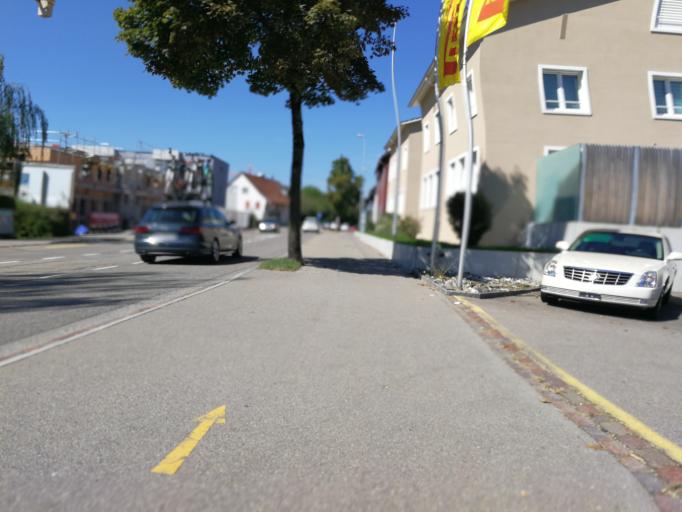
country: CH
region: Zurich
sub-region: Bezirk Pfaeffikon
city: Pfaeffikon / Irgenhausen
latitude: 47.3604
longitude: 8.7937
